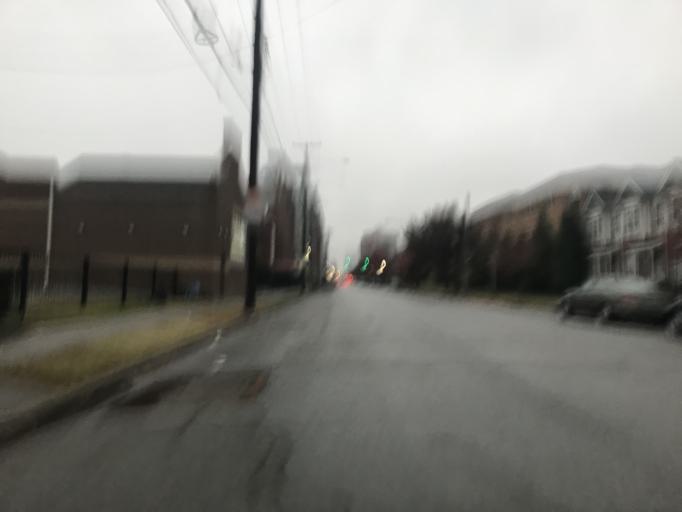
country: US
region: Kentucky
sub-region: Jefferson County
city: Louisville
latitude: 38.2492
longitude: -85.7395
